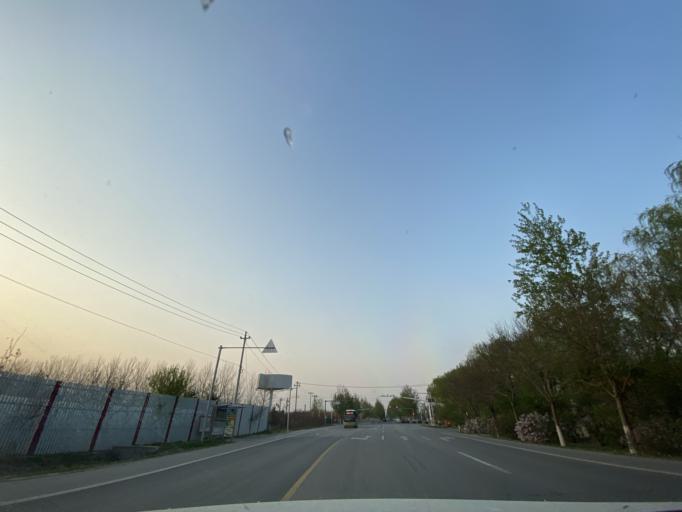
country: CN
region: Beijing
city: Weishanzhuang
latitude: 39.6144
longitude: 116.4095
